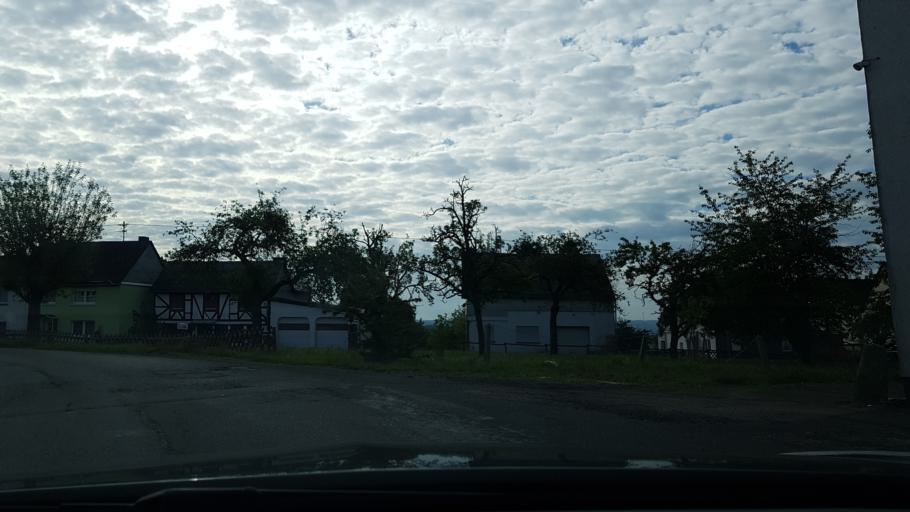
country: DE
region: Rheinland-Pfalz
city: Mermuth
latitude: 50.1589
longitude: 7.4802
